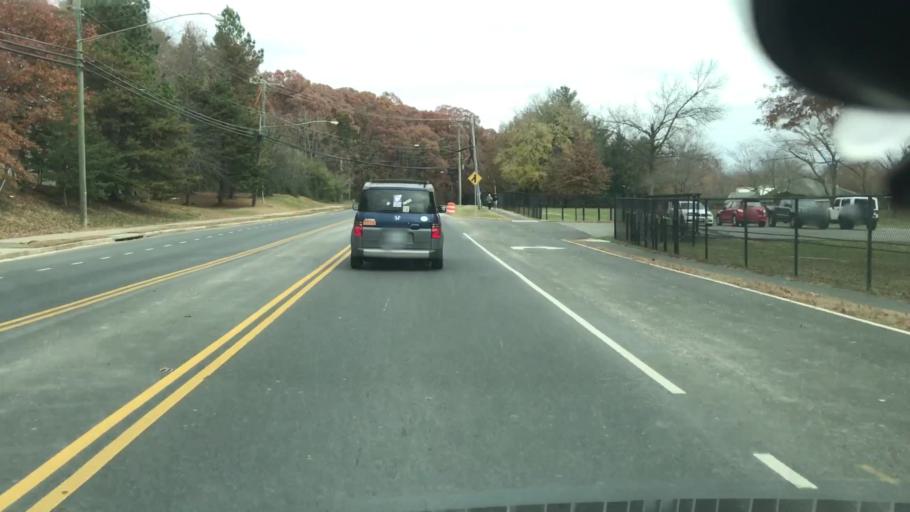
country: US
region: Virginia
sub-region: Fairfax County
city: Hayfield
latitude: 38.7587
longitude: -77.1353
